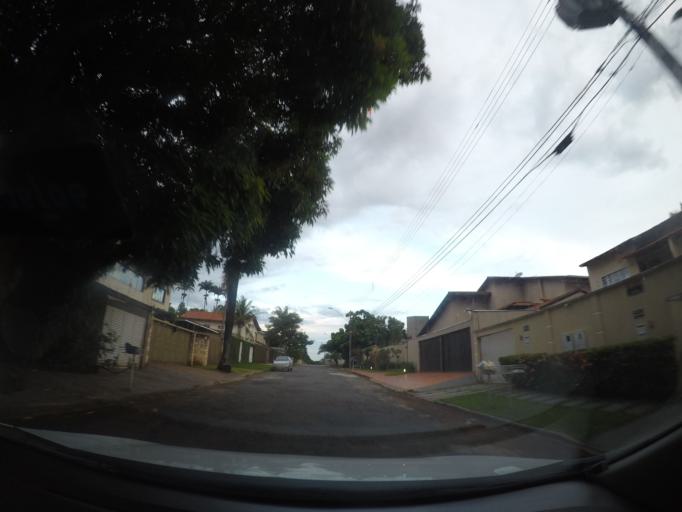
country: BR
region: Goias
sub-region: Goiania
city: Goiania
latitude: -16.6540
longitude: -49.2290
